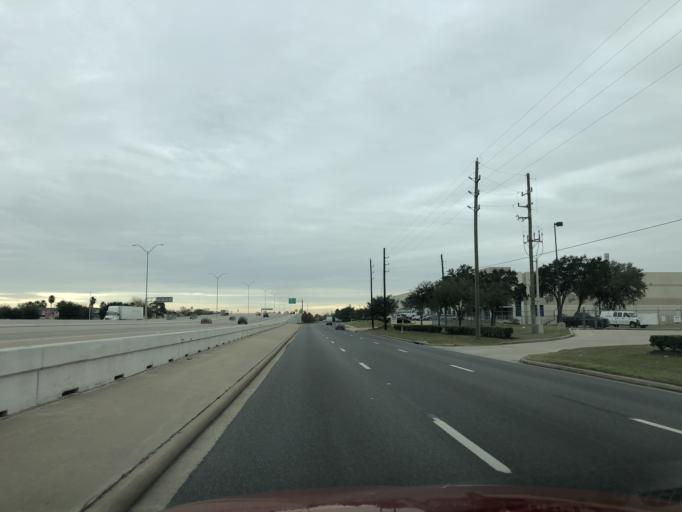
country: US
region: Texas
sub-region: Fort Bend County
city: Missouri City
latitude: 29.6400
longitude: -95.5347
